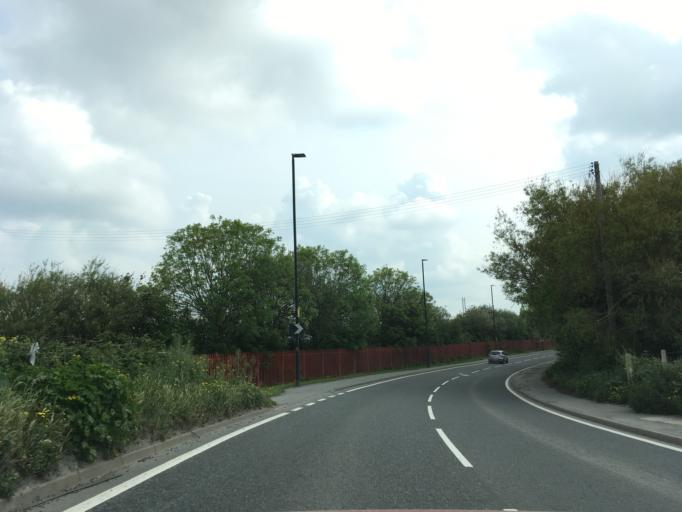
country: GB
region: England
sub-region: South Gloucestershire
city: Severn Beach
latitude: 51.5276
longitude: -2.6829
